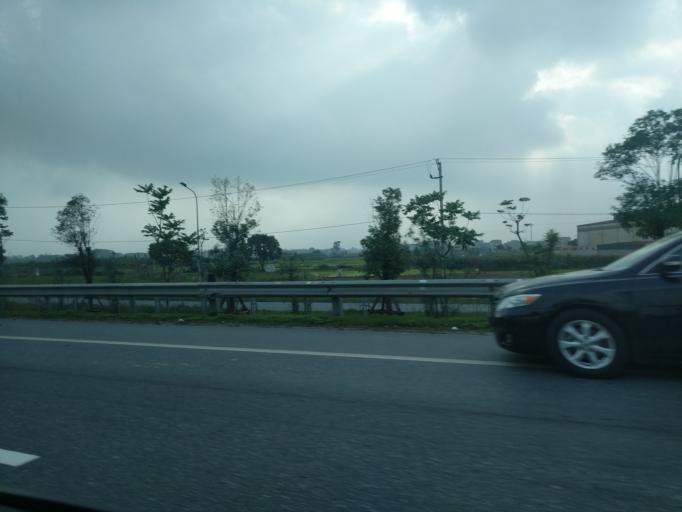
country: VN
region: Ha Noi
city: Dong Anh
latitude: 21.1814
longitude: 105.8280
